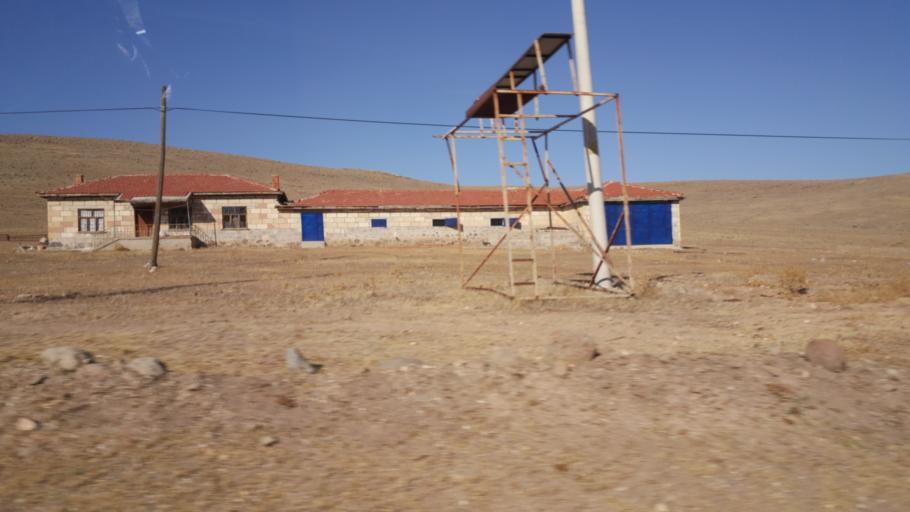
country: TR
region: Ankara
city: Altpinar
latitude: 39.1705
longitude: 32.6999
